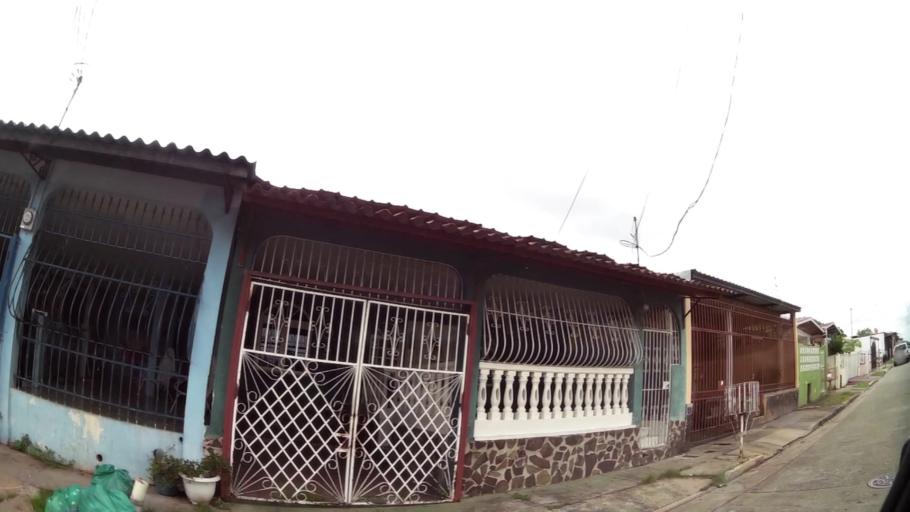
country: PA
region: Panama
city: Tocumen
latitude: 9.0549
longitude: -79.4093
